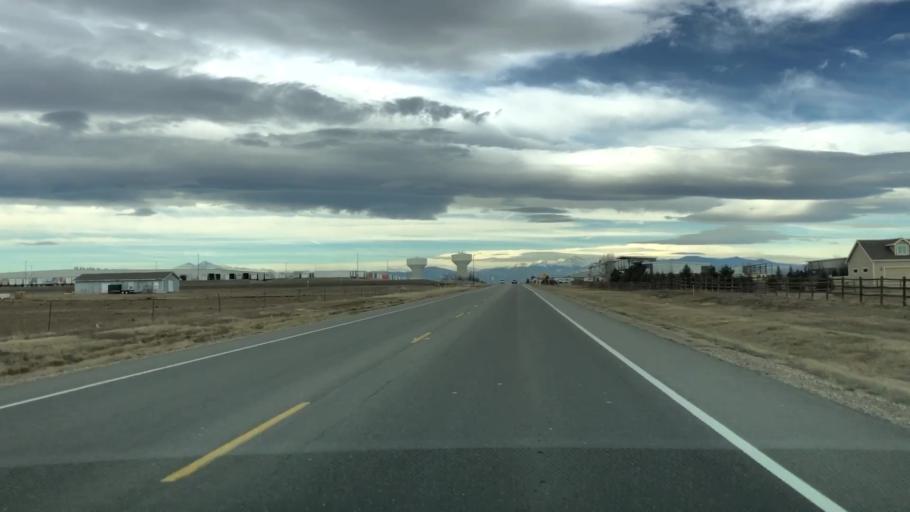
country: US
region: Colorado
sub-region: Weld County
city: Windsor
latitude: 40.4361
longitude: -104.9604
